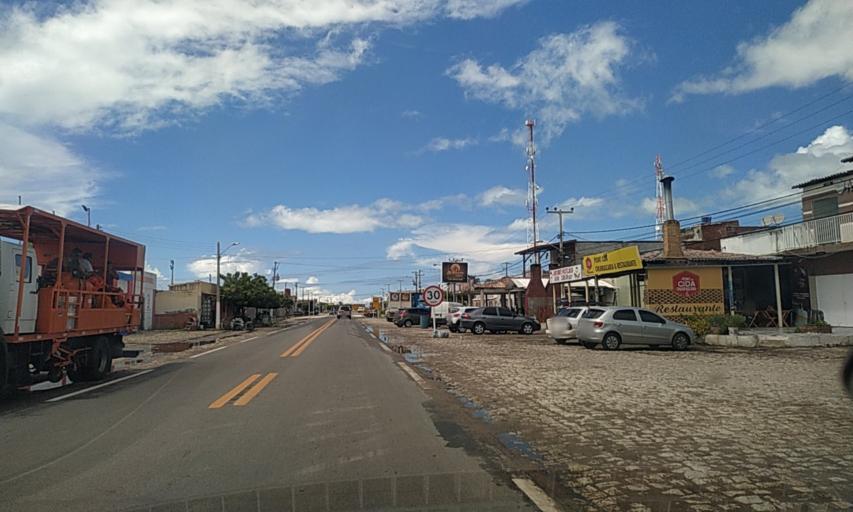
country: BR
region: Rio Grande do Norte
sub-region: Areia Branca
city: Areia Branca
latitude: -4.9537
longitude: -37.1290
